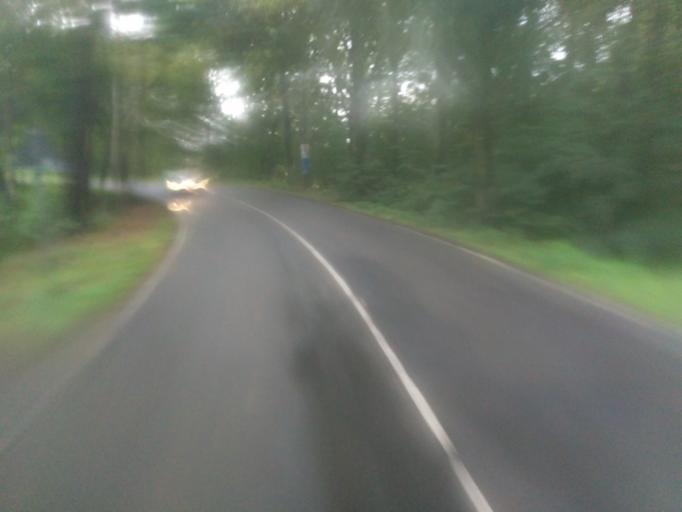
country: DE
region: Saxony
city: Lohsa
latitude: 51.3812
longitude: 14.4006
